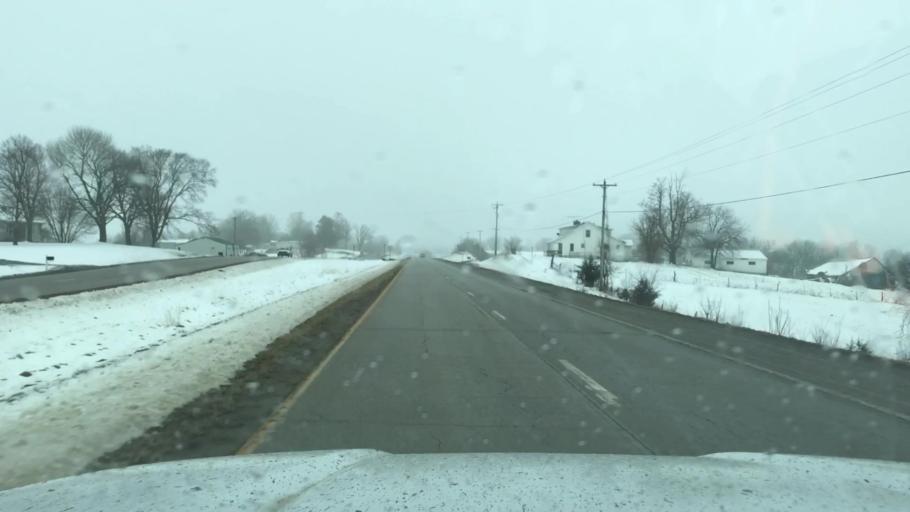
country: US
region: Missouri
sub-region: Andrew County
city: Country Club Village
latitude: 39.8732
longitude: -94.8090
